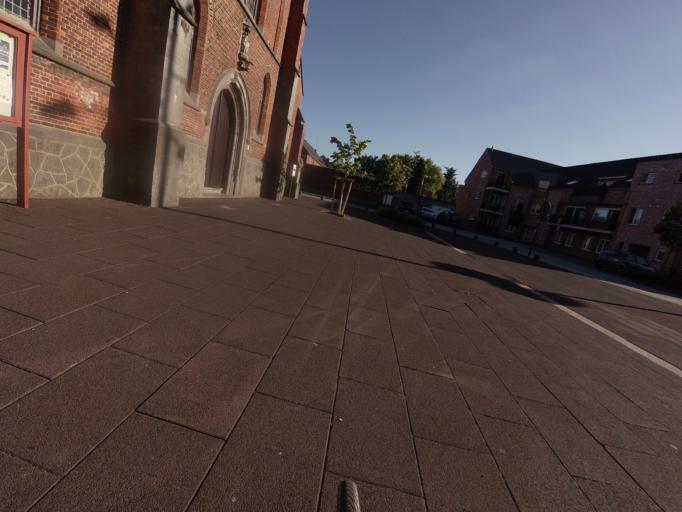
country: BE
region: Flanders
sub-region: Provincie Antwerpen
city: Rijkevorsel
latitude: 51.3292
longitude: 4.7822
